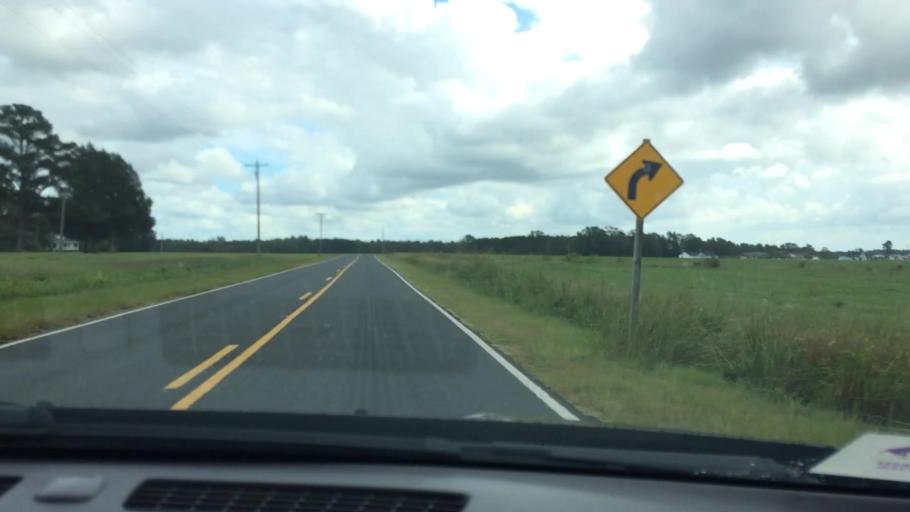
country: US
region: North Carolina
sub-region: Greene County
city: Maury
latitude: 35.5176
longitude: -77.5286
